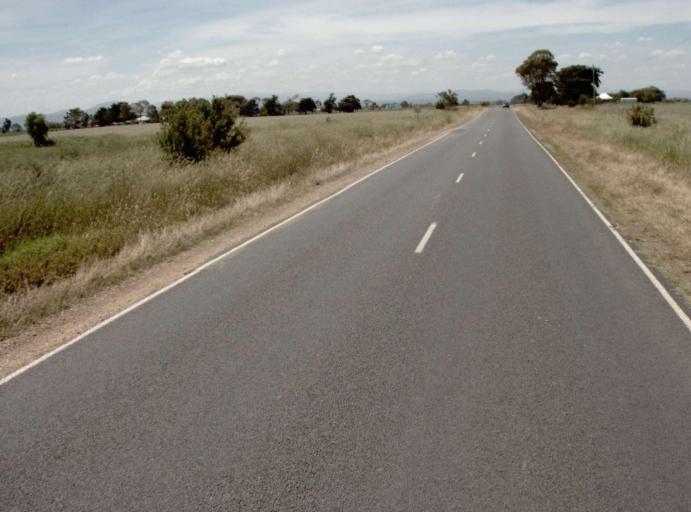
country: AU
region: Victoria
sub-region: Wellington
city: Heyfield
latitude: -38.0025
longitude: 146.8839
